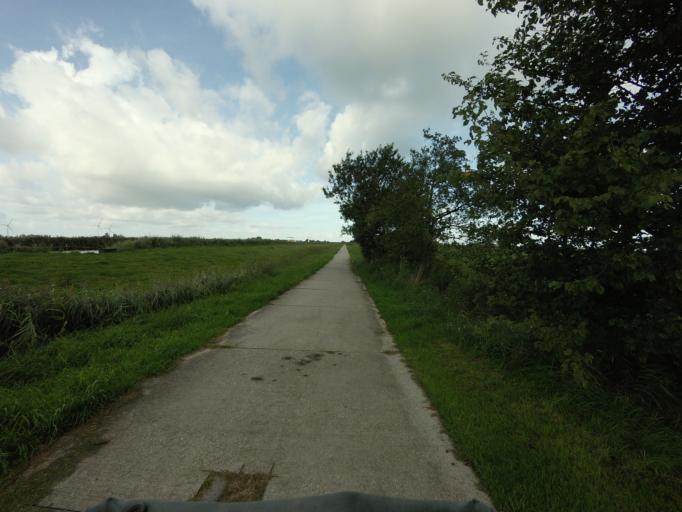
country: NL
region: Friesland
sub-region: Sudwest Fryslan
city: Makkum
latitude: 53.0515
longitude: 5.4495
